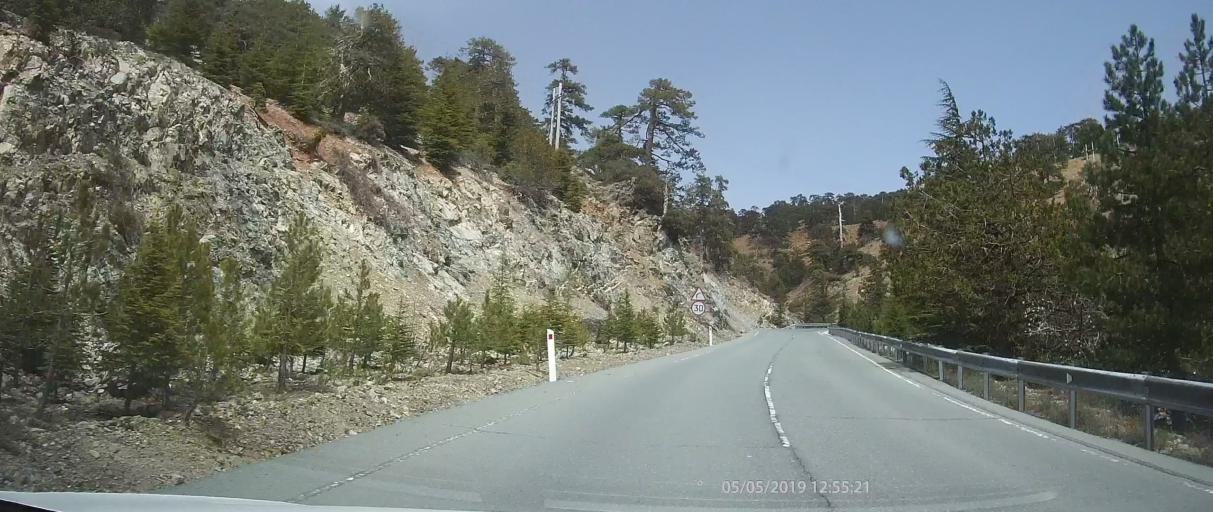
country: CY
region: Lefkosia
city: Kakopetria
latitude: 34.9442
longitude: 32.8537
